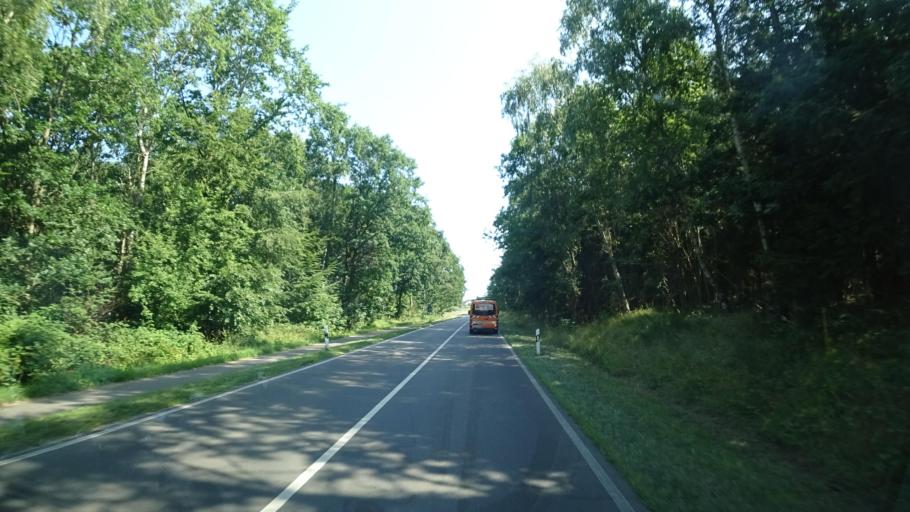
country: DE
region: Mecklenburg-Vorpommern
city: Kroslin
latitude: 54.1393
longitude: 13.6907
